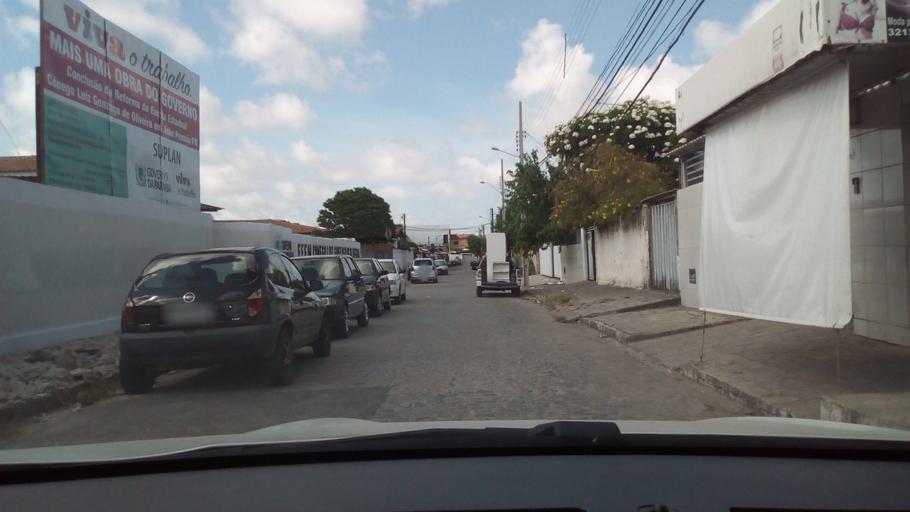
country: BR
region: Paraiba
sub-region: Joao Pessoa
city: Joao Pessoa
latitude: -7.1716
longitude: -34.8381
